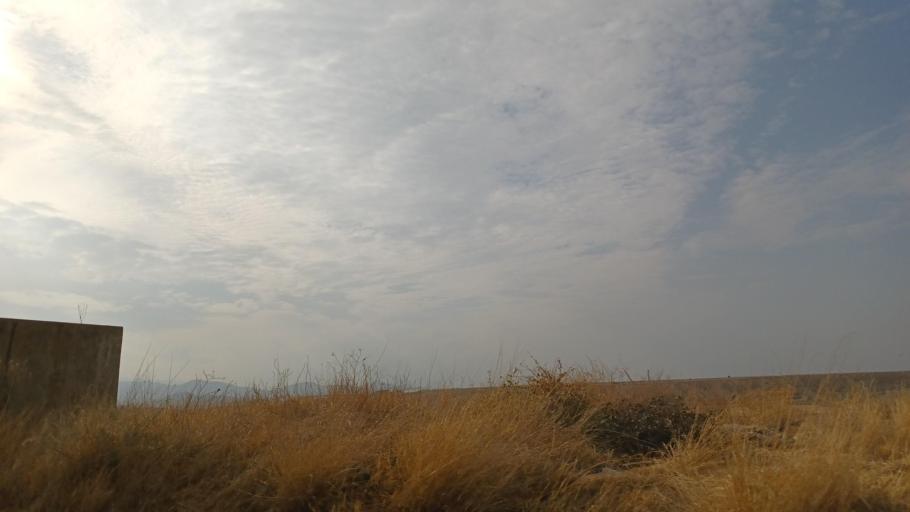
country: CY
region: Lefkosia
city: Peristerona
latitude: 35.0834
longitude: 33.0936
